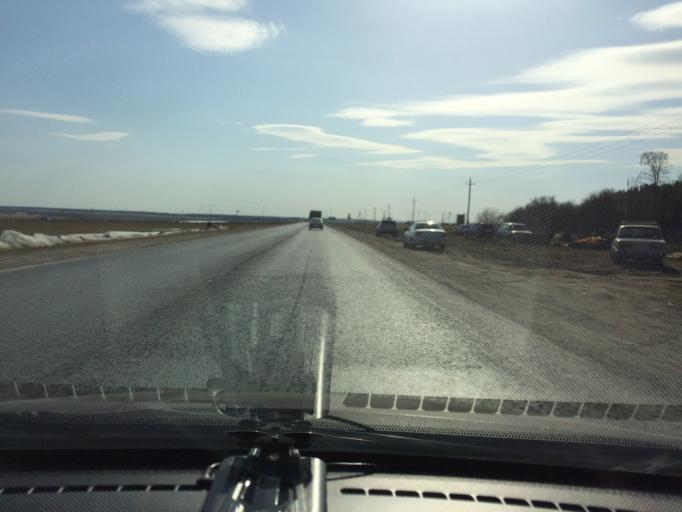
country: RU
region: Mariy-El
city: Yoshkar-Ola
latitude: 56.6992
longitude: 48.0653
